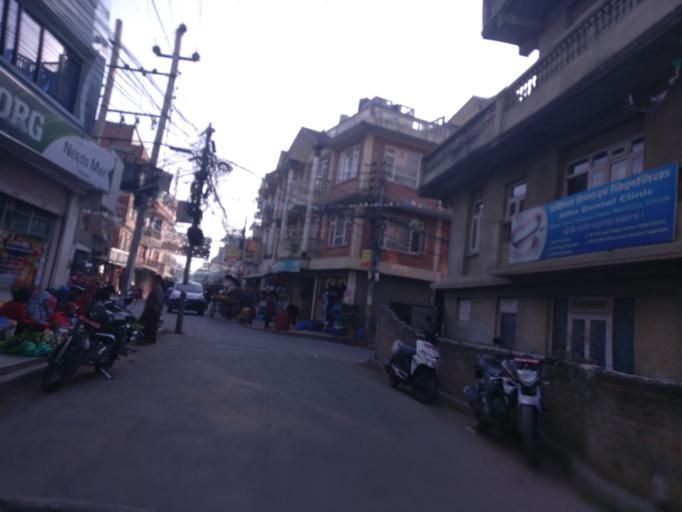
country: NP
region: Central Region
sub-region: Bagmati Zone
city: Patan
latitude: 27.6546
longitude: 85.3196
